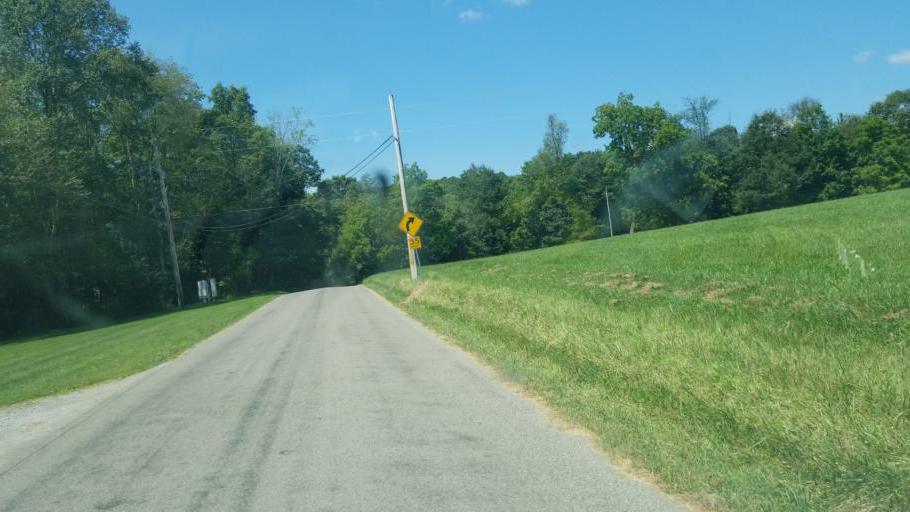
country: US
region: Pennsylvania
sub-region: Clarion County
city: Knox
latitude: 41.1812
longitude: -79.5021
